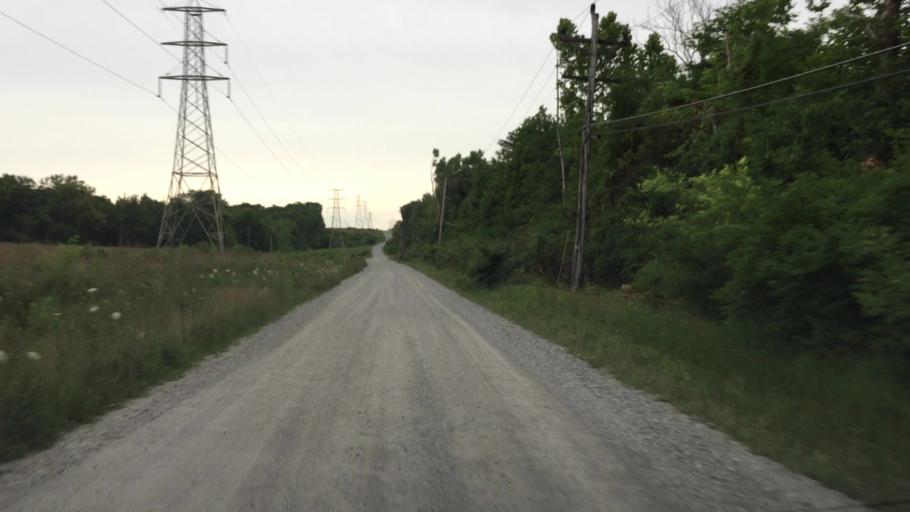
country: US
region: Illinois
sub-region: Hancock County
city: Hamilton
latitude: 40.3631
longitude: -91.3612
